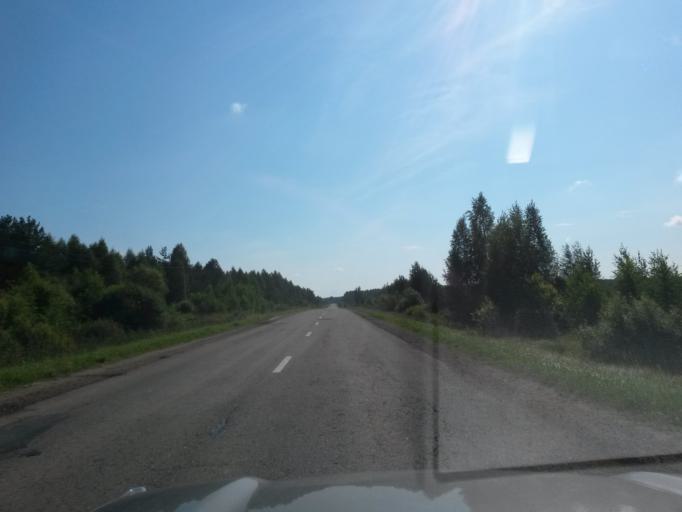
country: RU
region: Jaroslavl
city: Gavrilov-Yam
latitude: 57.3081
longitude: 39.9663
